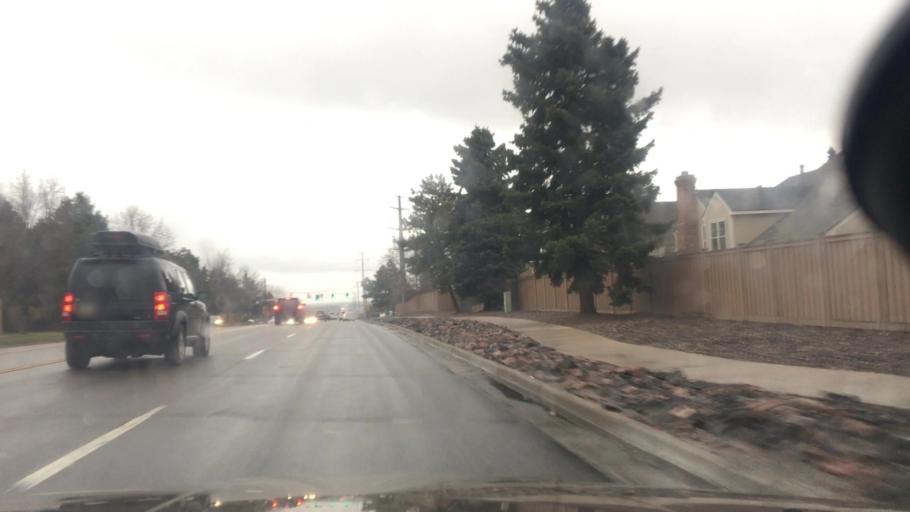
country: US
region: Colorado
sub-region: Arapahoe County
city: Castlewood
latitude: 39.5786
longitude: -104.9229
